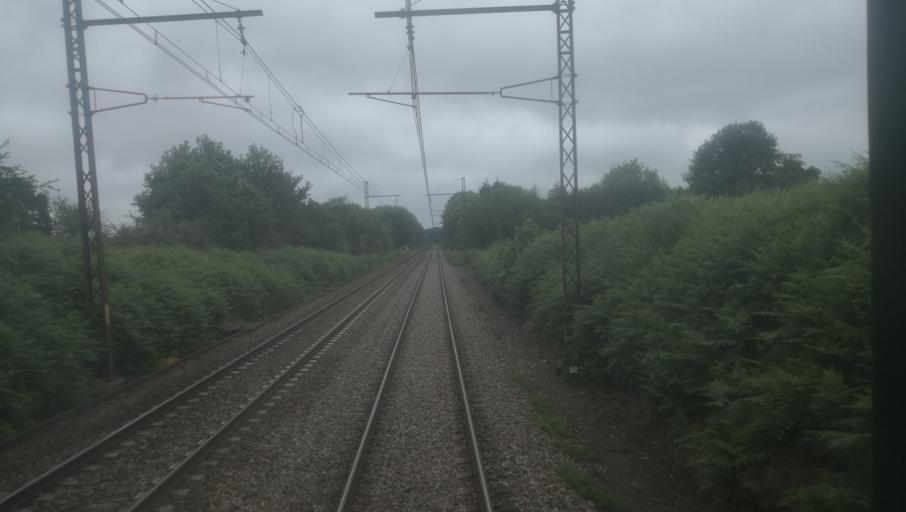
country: FR
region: Limousin
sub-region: Departement de la Creuse
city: La Souterraine
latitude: 46.2648
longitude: 1.4739
